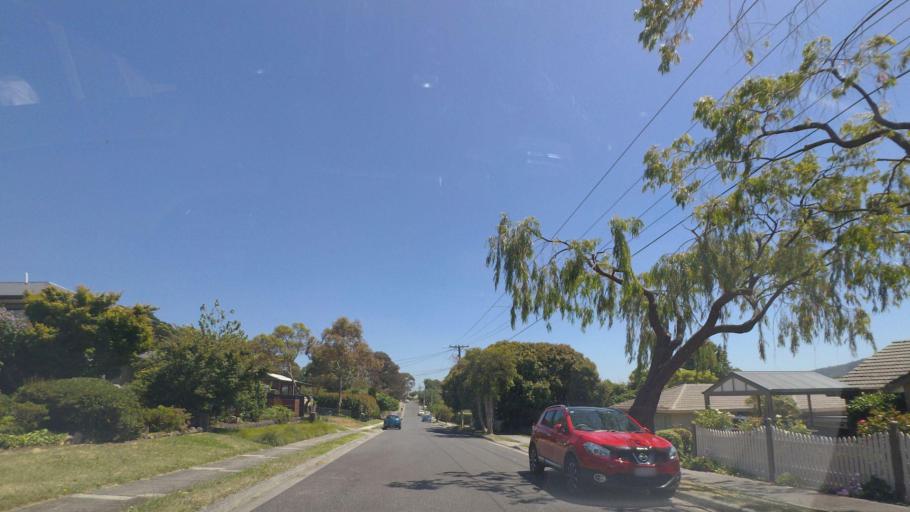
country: AU
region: Victoria
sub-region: Knox
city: Ferntree Gully
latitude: -37.8961
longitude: 145.2906
